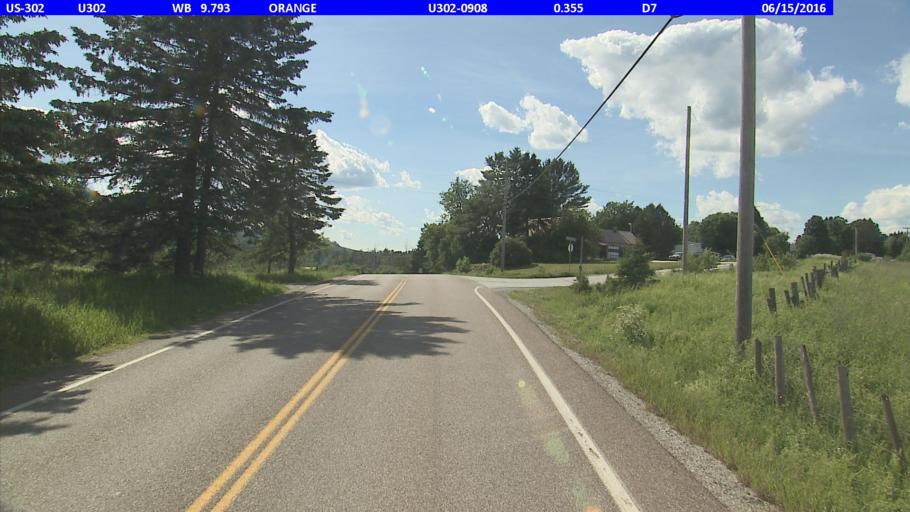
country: US
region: Vermont
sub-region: Washington County
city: South Barre
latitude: 44.1525
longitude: -72.4299
